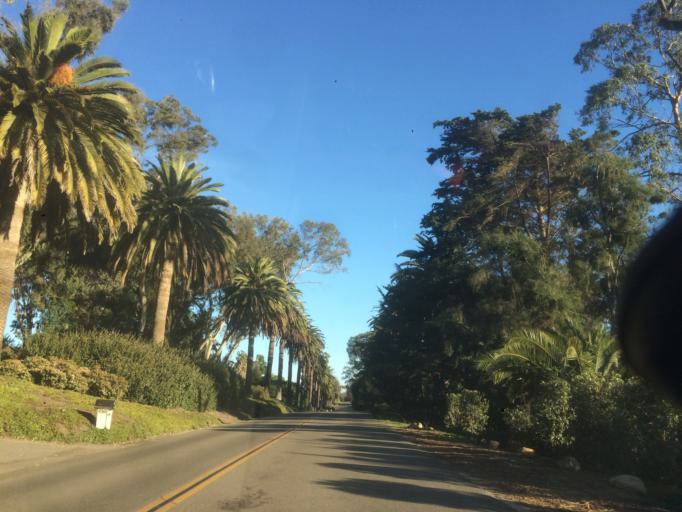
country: US
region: California
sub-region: Santa Barbara County
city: Mission Canyon
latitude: 34.4108
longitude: -119.7619
